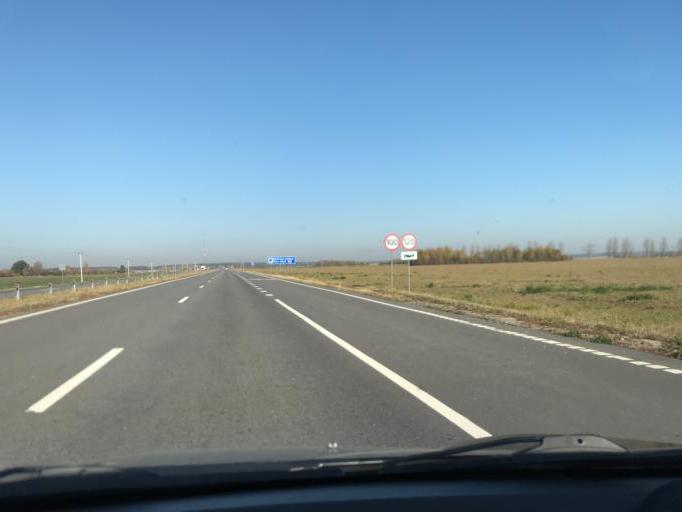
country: BY
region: Mogilev
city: Babruysk
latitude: 53.1648
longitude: 29.3601
